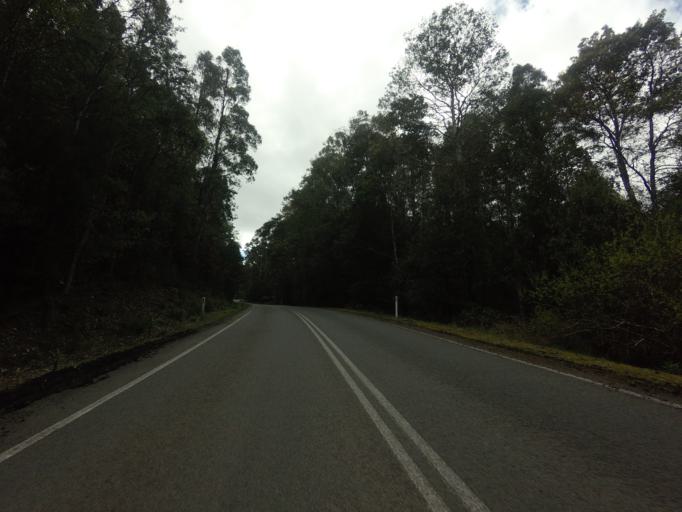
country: AU
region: Tasmania
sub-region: Huon Valley
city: Geeveston
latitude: -43.4064
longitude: 146.9585
